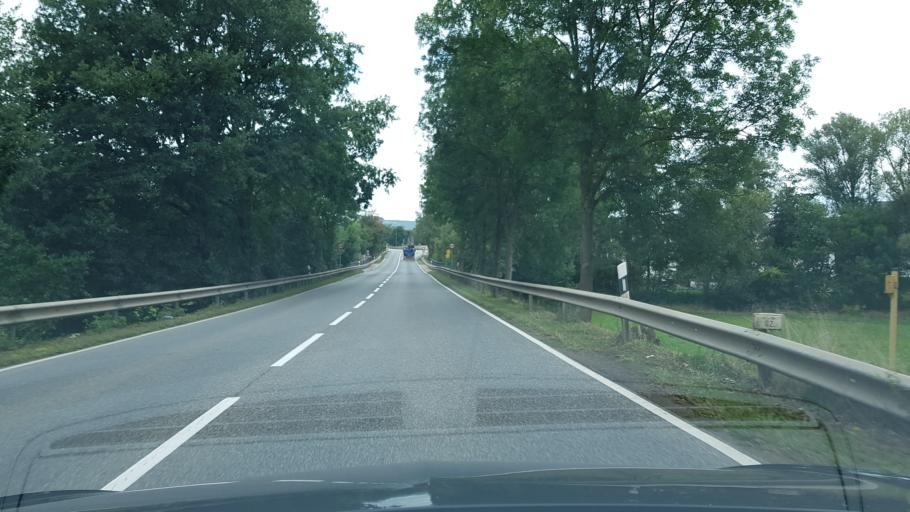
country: DE
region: Rheinland-Pfalz
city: Plaidt
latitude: 50.3864
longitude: 7.3858
